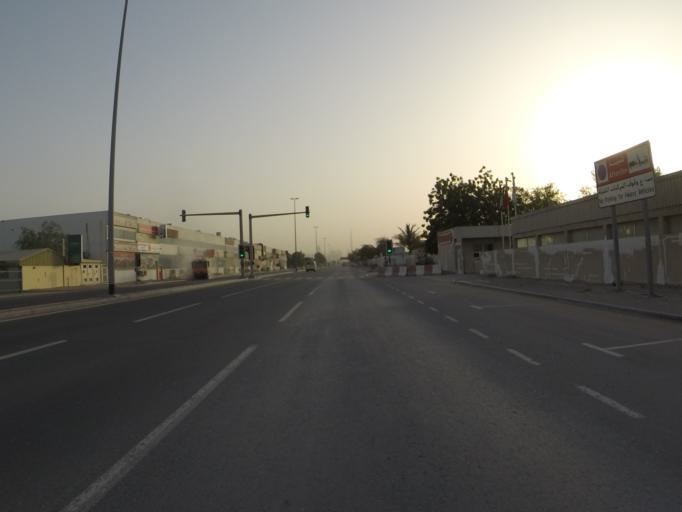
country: AE
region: Dubai
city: Dubai
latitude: 25.1307
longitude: 55.2187
